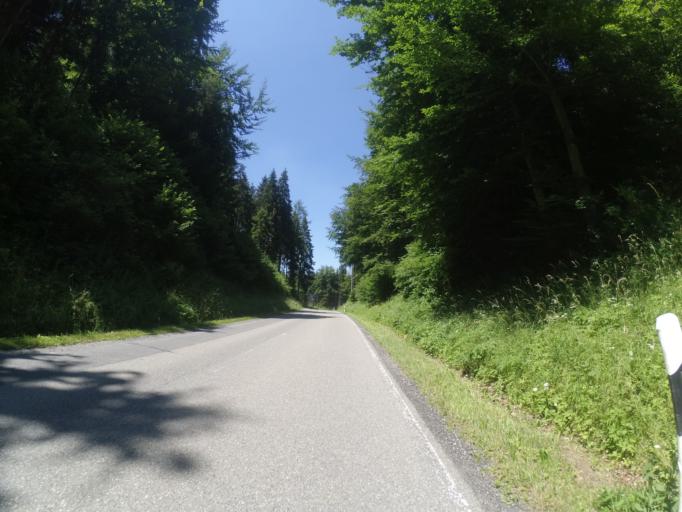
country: DE
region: Baden-Wuerttemberg
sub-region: Tuebingen Region
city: Bad Waldsee
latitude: 47.9059
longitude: 9.7776
